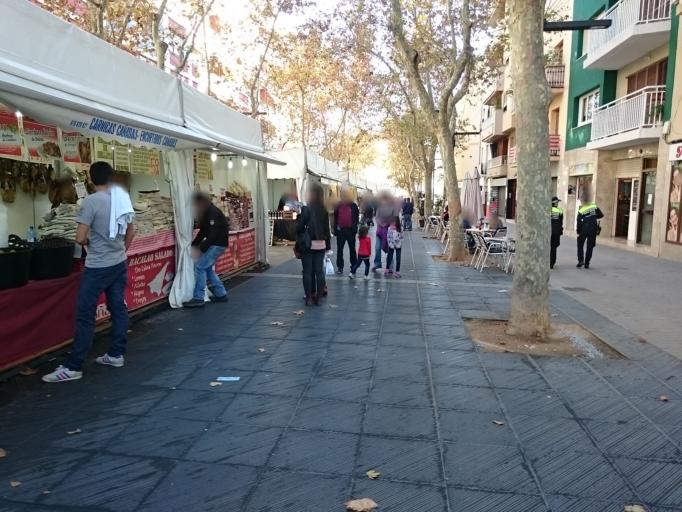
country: ES
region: Catalonia
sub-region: Provincia de Barcelona
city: Vilanova i la Geltru
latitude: 41.2167
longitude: 1.7290
